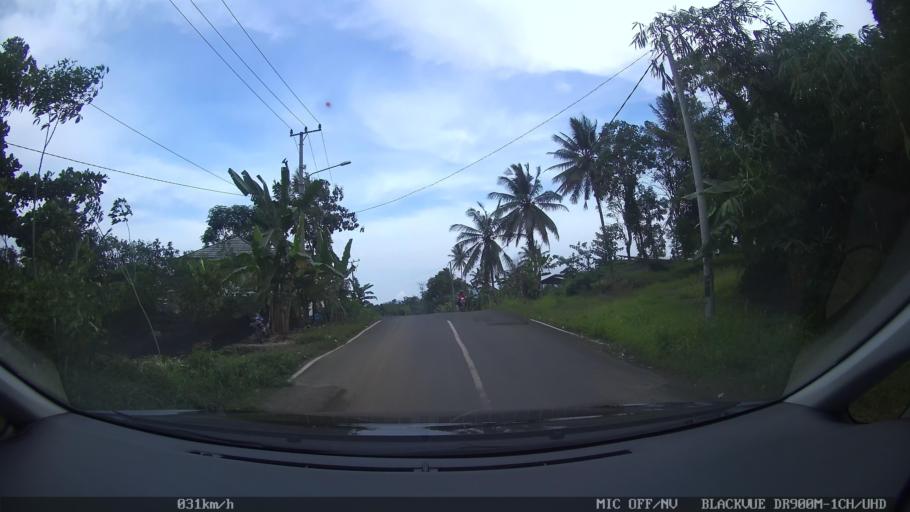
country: ID
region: Lampung
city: Bandarlampung
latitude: -5.4243
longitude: 105.1950
